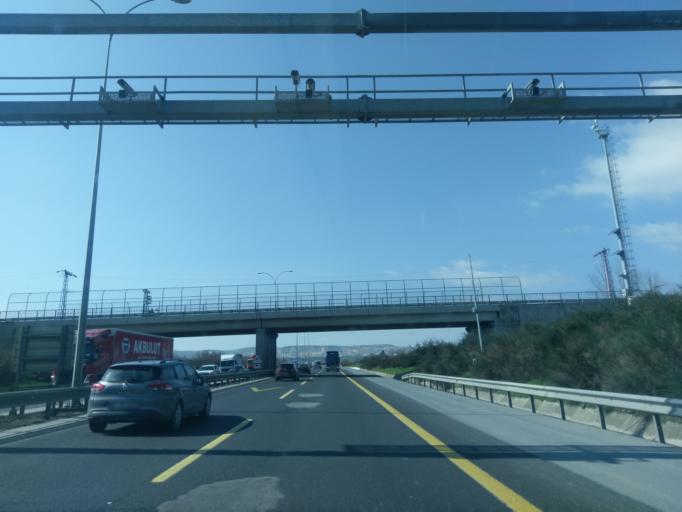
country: TR
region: Istanbul
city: Muratbey
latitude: 41.1066
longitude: 28.5472
